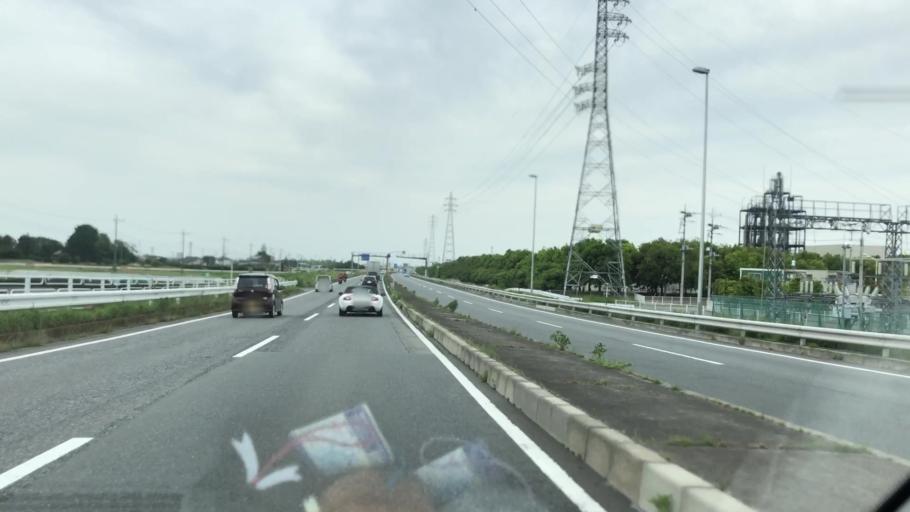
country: JP
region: Gunma
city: Sakai-nakajima
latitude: 36.2710
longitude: 139.2869
